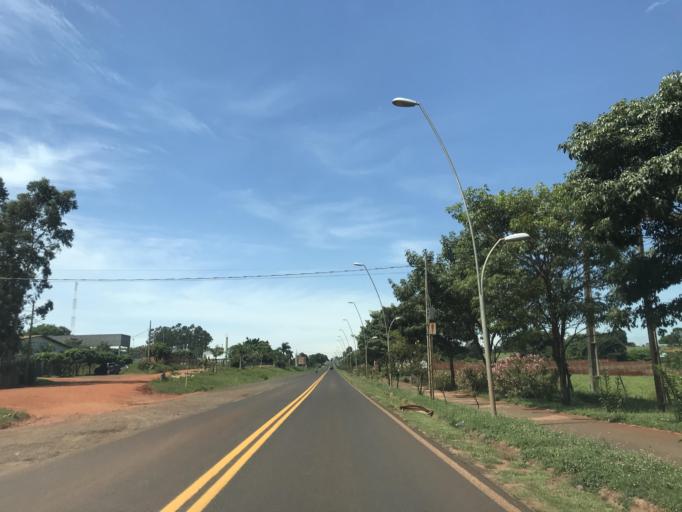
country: BR
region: Parana
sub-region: Terra Rica
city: Terra Rica
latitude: -22.7401
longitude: -52.6248
